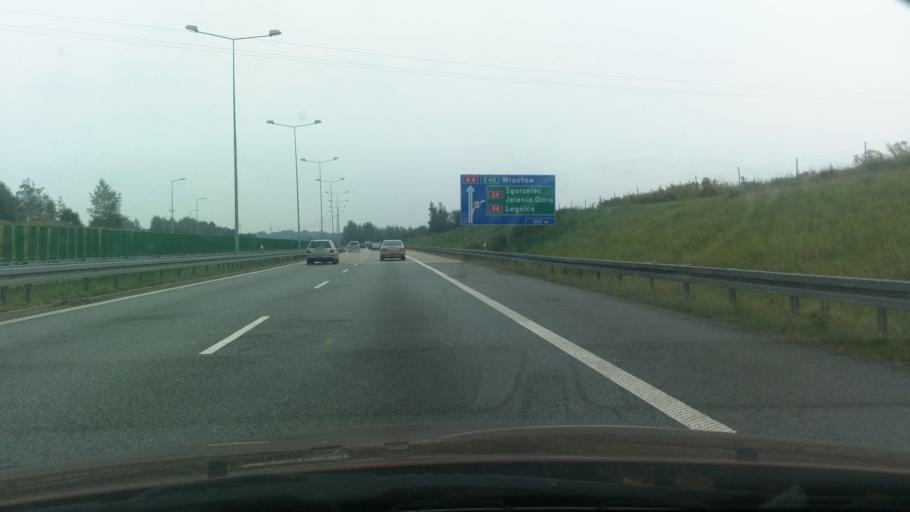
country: PL
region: Lower Silesian Voivodeship
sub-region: Powiat zgorzelecki
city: Lagow
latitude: 51.1750
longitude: 15.0223
